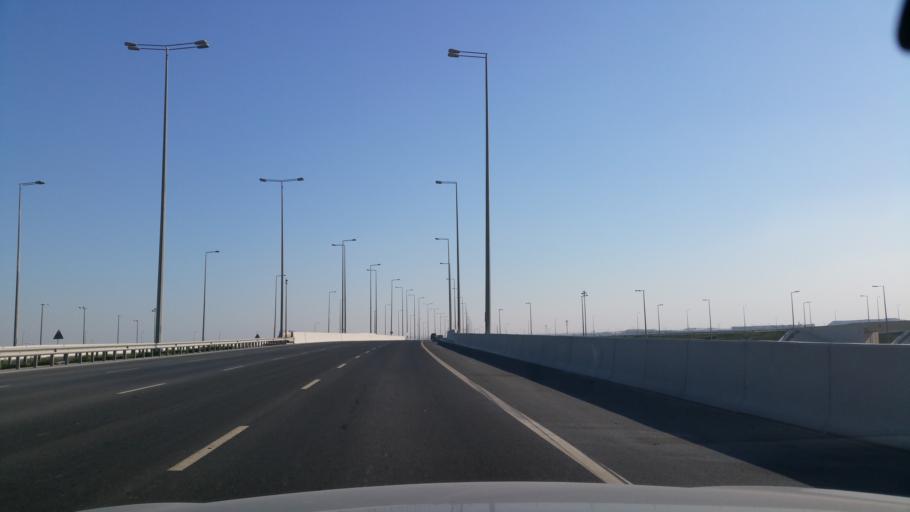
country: QA
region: Al Wakrah
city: Al Wukayr
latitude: 25.1674
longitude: 51.4715
